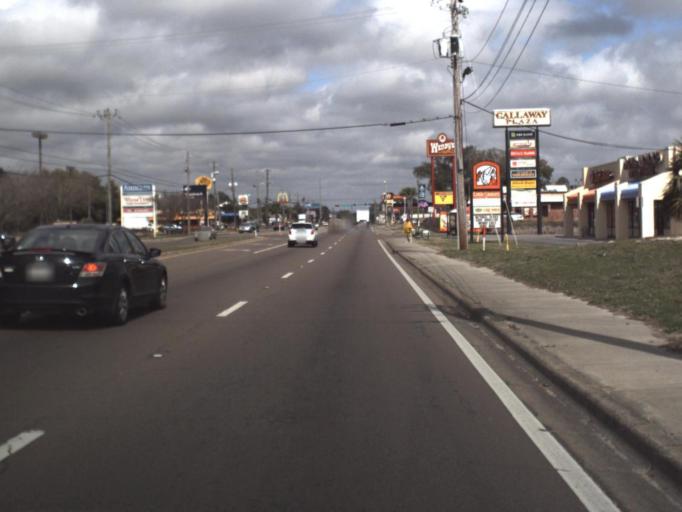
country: US
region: Florida
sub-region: Bay County
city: Parker
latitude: 30.1434
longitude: -85.5911
